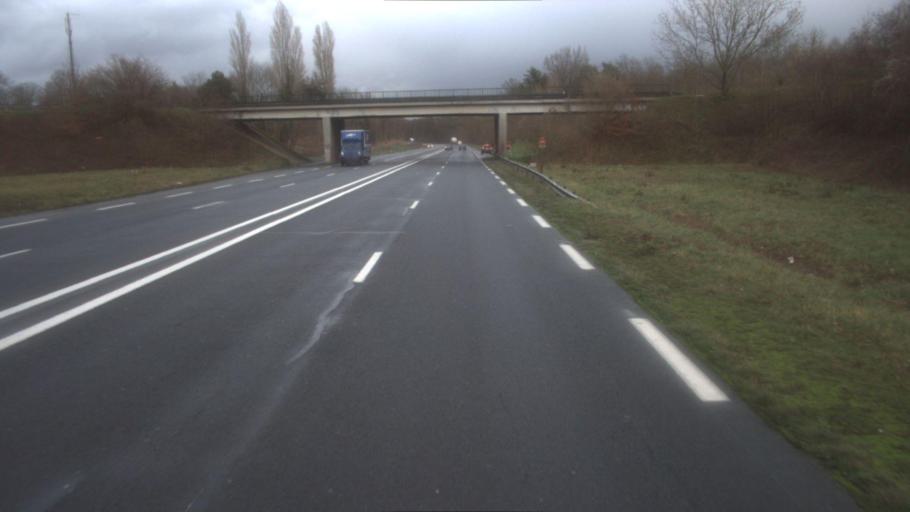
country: FR
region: Ile-de-France
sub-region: Departement de Seine-et-Marne
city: Cely
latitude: 48.4679
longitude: 2.5391
